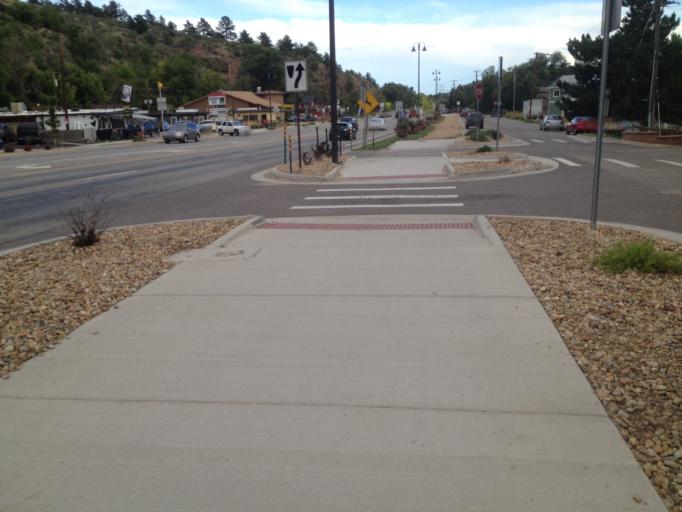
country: US
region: Colorado
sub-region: Boulder County
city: Lyons
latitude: 40.2227
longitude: -105.2656
